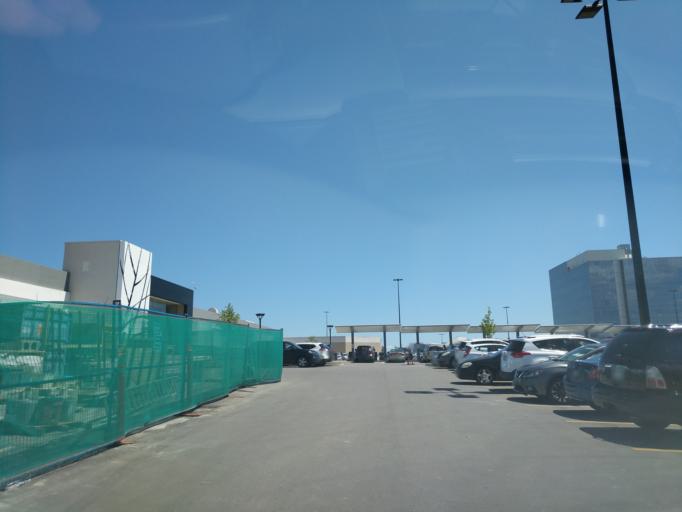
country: CA
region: Ontario
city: Ajax
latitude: 43.8352
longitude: -79.0868
